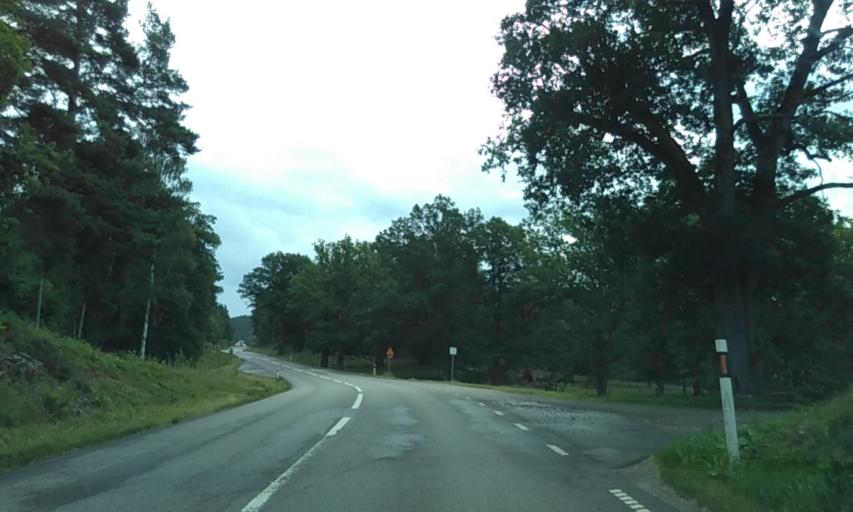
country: SE
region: Vaestra Goetaland
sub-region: Alingsas Kommun
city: Alingsas
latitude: 57.9574
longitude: 12.4517
